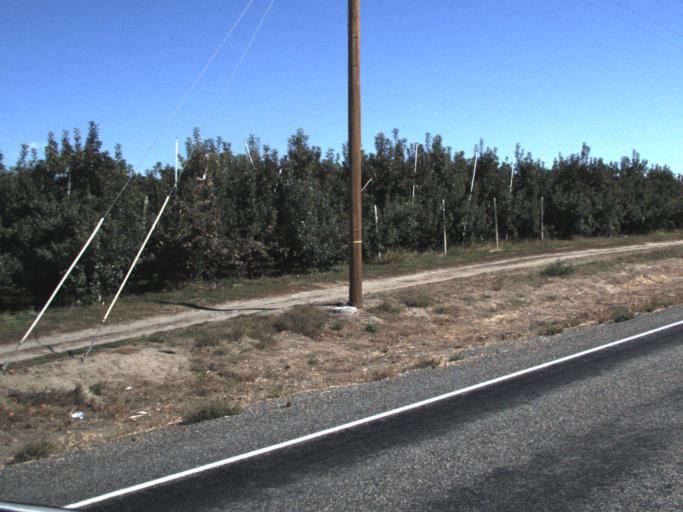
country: US
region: Washington
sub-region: Walla Walla County
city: Burbank
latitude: 46.2118
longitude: -118.9608
